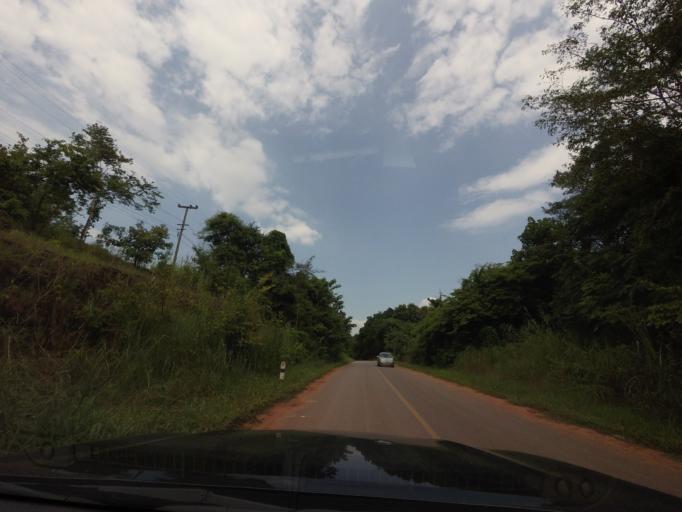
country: TH
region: Uttaradit
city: Fak Tha
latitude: 17.8268
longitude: 100.9412
